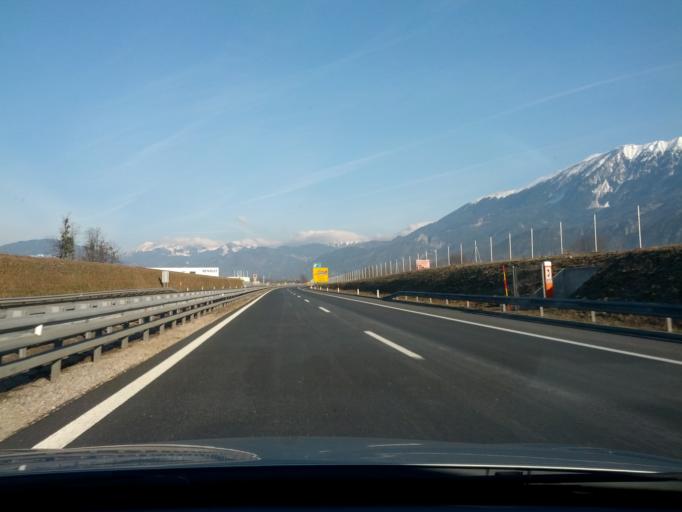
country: SI
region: Radovljica
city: Lesce
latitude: 46.3633
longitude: 14.1653
